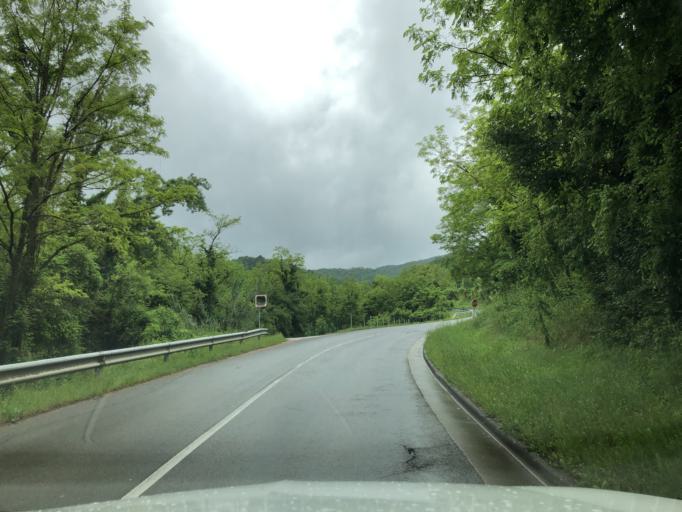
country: SI
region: Koper-Capodistria
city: Prade
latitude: 45.5139
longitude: 13.7799
